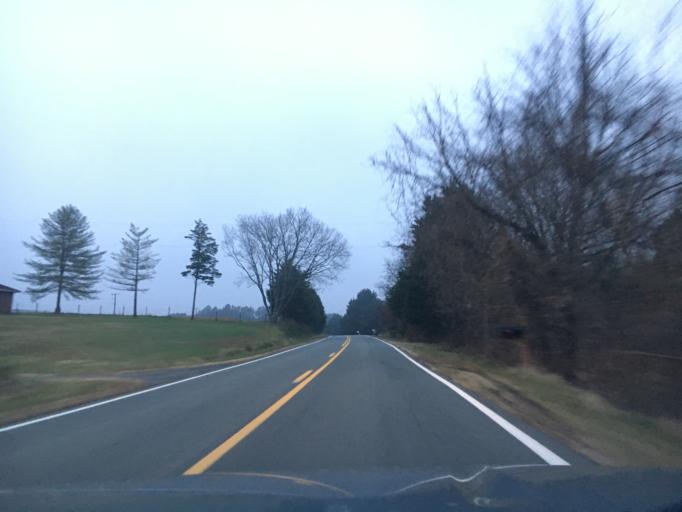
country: US
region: Virginia
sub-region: Halifax County
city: South Boston
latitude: 36.7011
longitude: -78.9599
